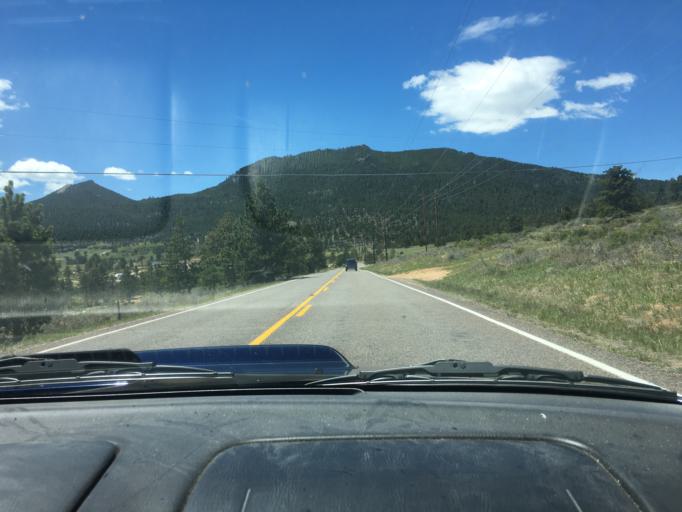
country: US
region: Colorado
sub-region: Larimer County
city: Estes Park
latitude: 40.3510
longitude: -105.5288
